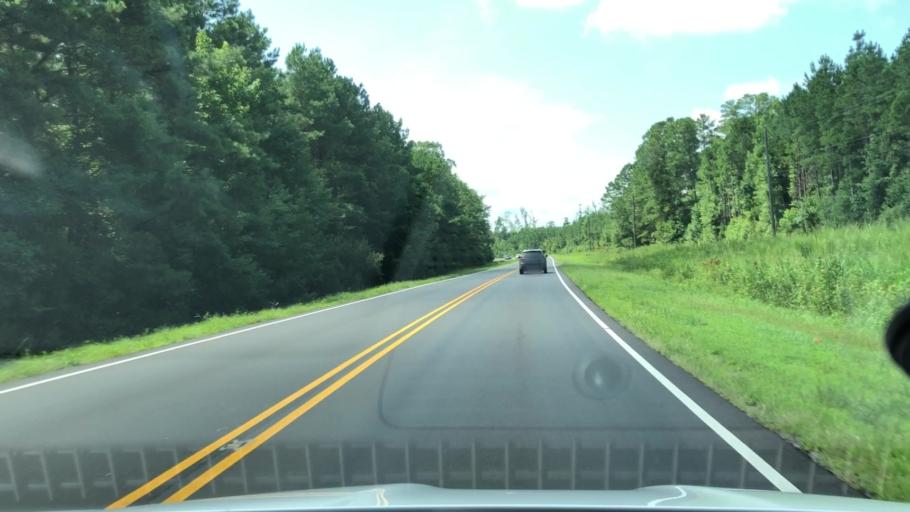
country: US
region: North Carolina
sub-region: Martin County
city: Williamston
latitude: 35.7329
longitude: -77.0754
